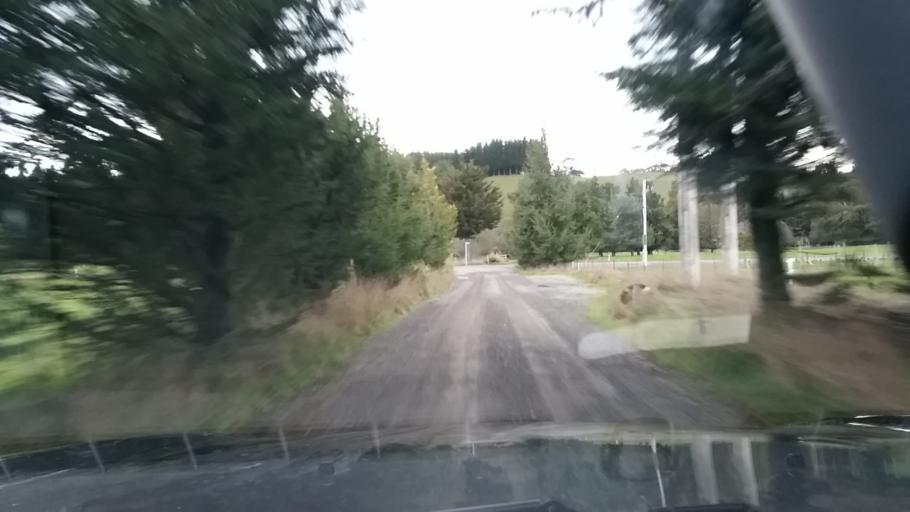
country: NZ
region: Marlborough
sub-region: Marlborough District
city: Blenheim
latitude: -41.5378
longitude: 173.6149
